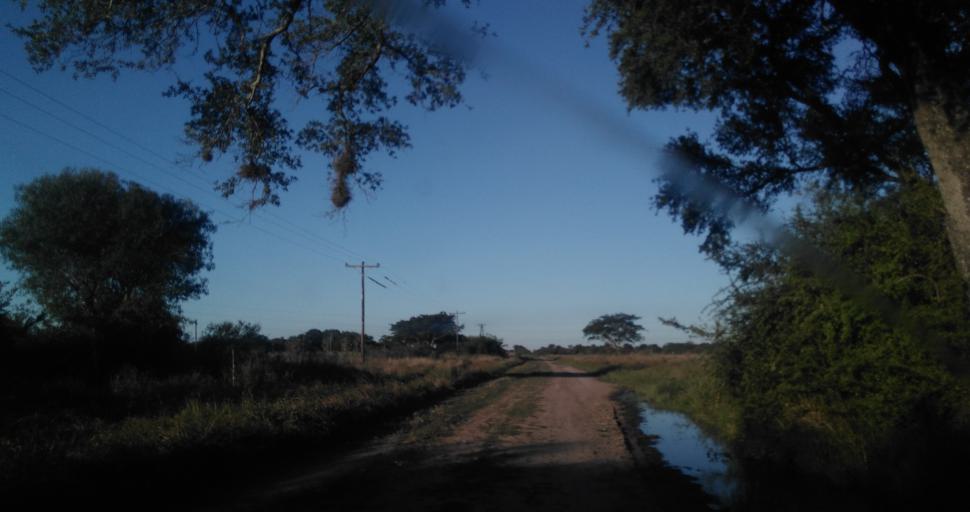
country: AR
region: Chaco
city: Fontana
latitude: -27.3911
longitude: -58.9788
